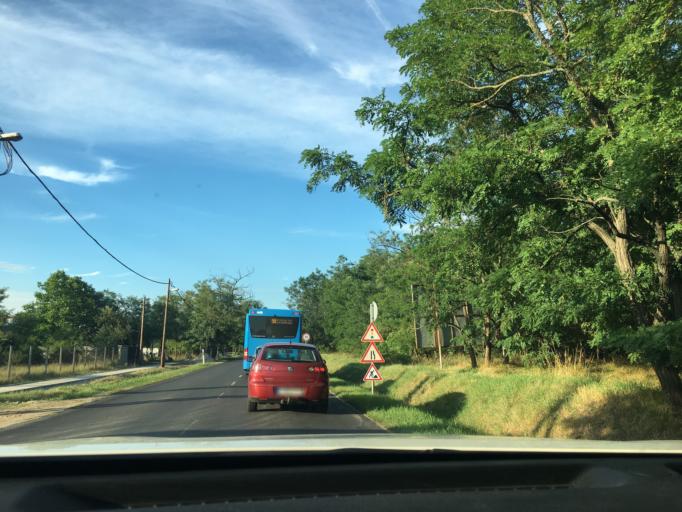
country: HU
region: Budapest
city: Budapest XVII. keruelet
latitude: 47.4518
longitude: 19.2273
